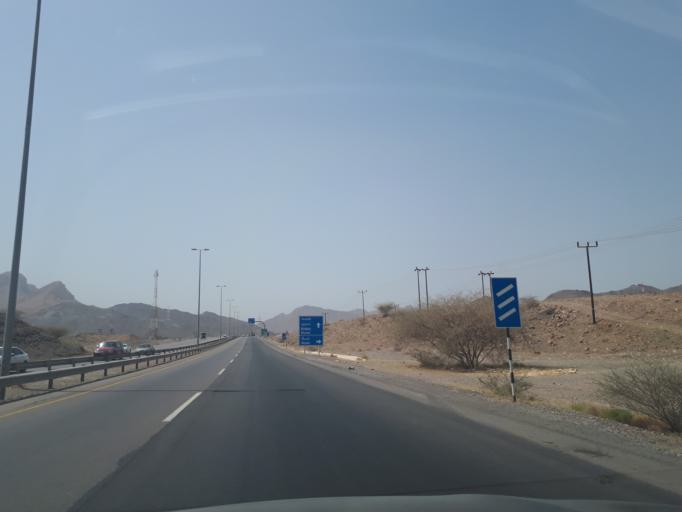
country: OM
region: Muhafazat ad Dakhiliyah
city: Bidbid
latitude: 23.4906
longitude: 58.1964
